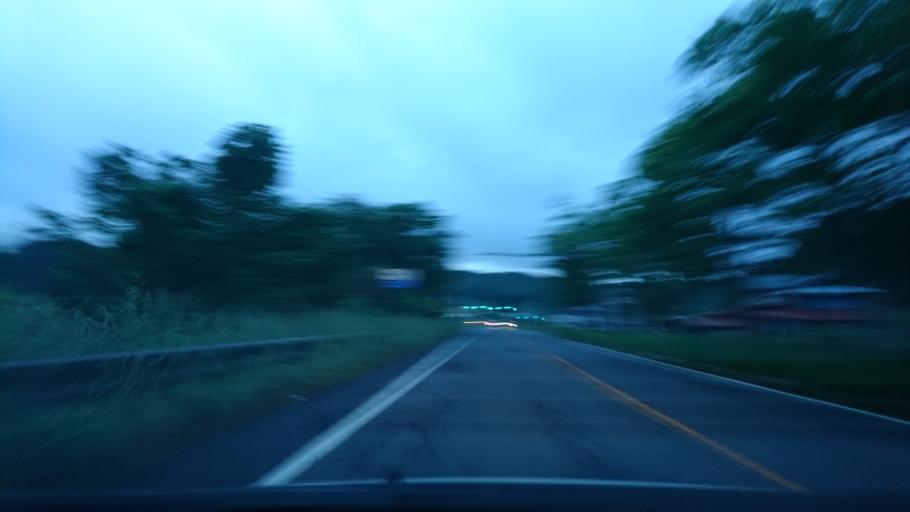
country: JP
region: Iwate
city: Ichinoseki
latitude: 38.8348
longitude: 141.0860
